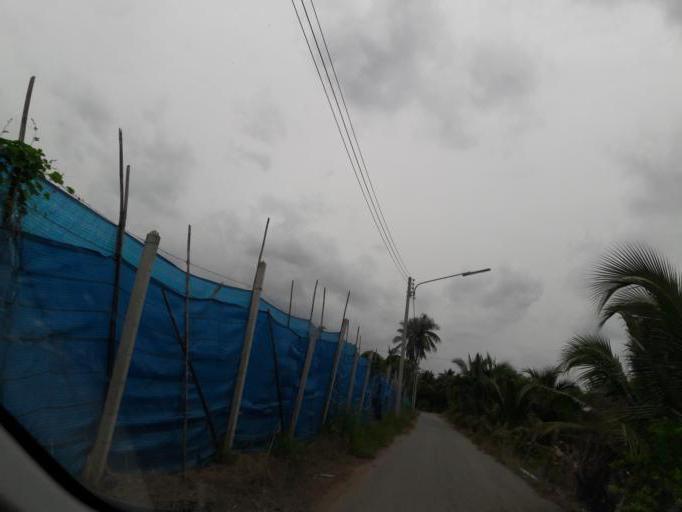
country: TH
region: Samut Sakhon
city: Ban Phaeo
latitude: 13.6140
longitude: 100.0233
